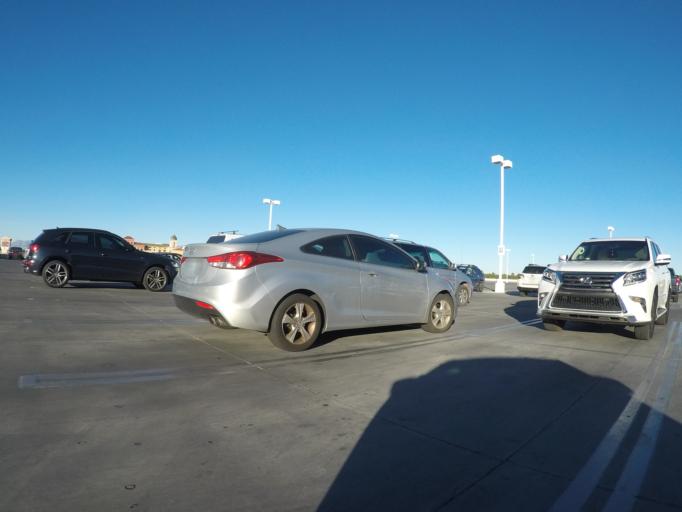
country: US
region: Nevada
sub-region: Clark County
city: Summerlin South
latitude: 36.1640
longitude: -115.2879
